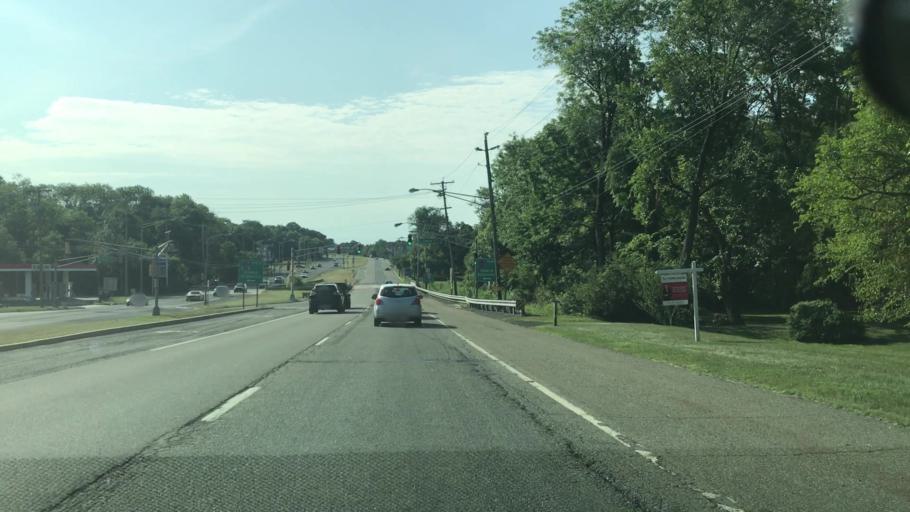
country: US
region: New Jersey
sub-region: Hunterdon County
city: Whitehouse Station
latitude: 40.6242
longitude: -74.7687
